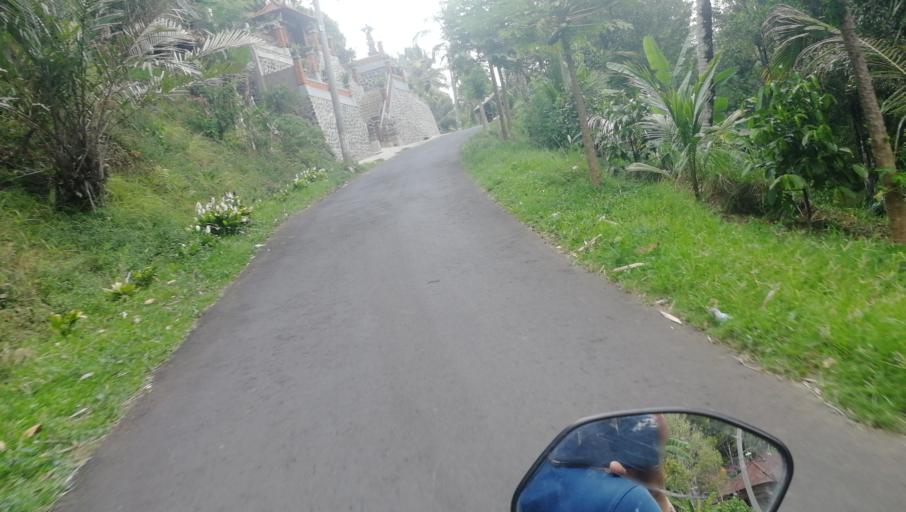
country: ID
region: Bali
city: Munduk
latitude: -8.2871
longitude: 115.0394
